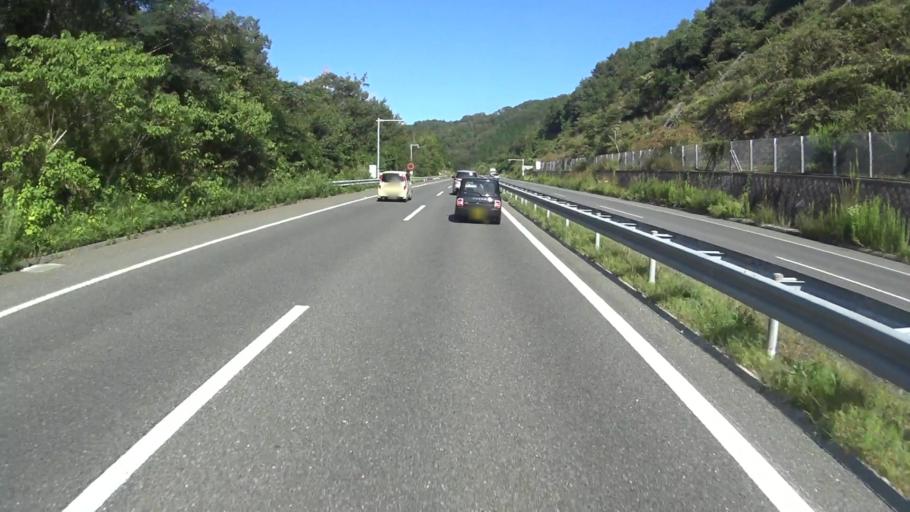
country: JP
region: Kyoto
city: Kameoka
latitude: 35.0968
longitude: 135.4970
